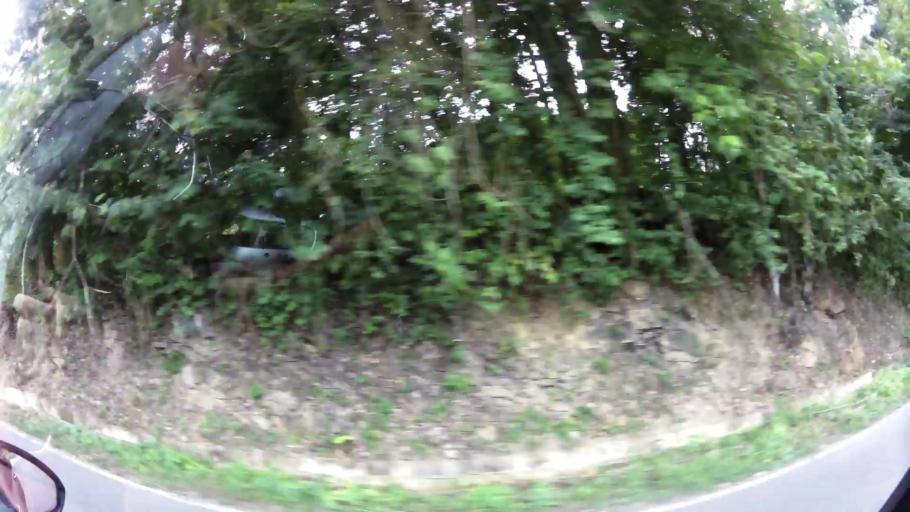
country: TT
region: Diego Martin
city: Petit Valley
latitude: 10.7240
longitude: -61.4945
